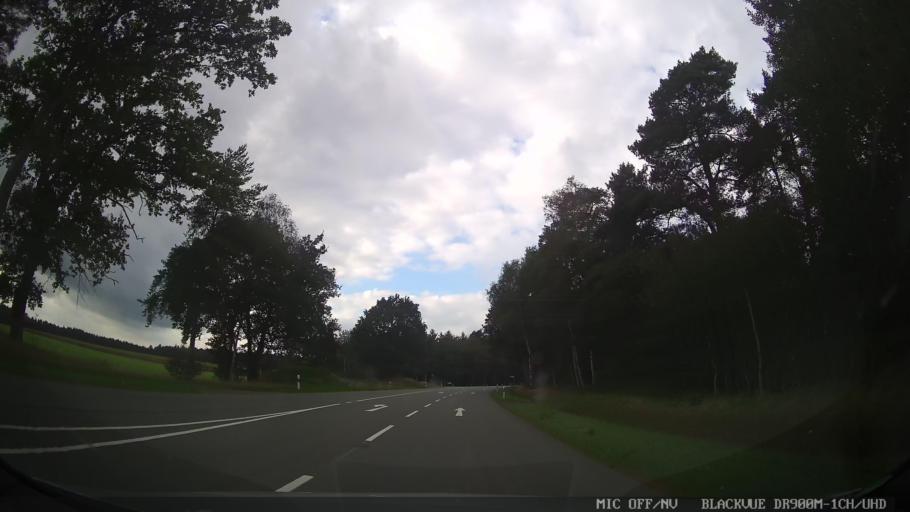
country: DE
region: Lower Saxony
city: Wietzendorf
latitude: 52.9641
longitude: 9.9607
